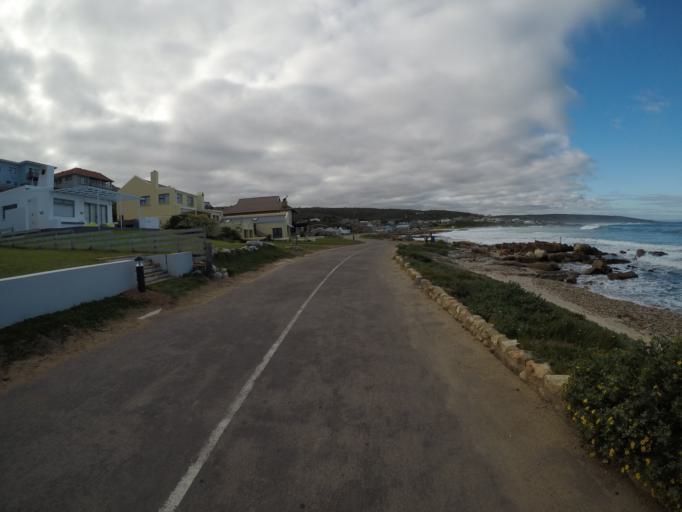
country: ZA
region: Western Cape
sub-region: Eden District Municipality
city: Riversdale
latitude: -34.4306
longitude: 21.3351
